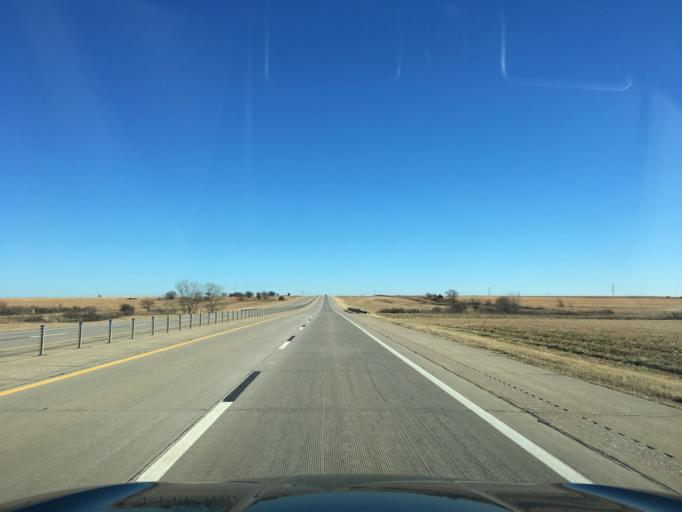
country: US
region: Oklahoma
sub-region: Noble County
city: Perry
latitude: 36.3921
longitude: -97.1286
